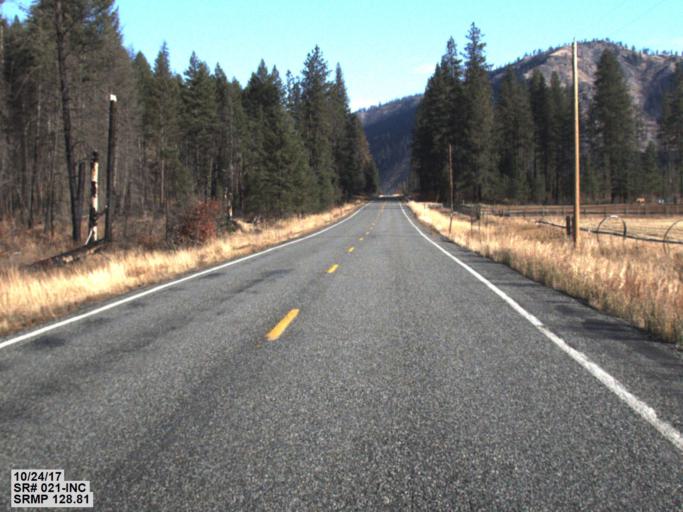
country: US
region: Washington
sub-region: Okanogan County
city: Coulee Dam
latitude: 48.2438
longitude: -118.6939
